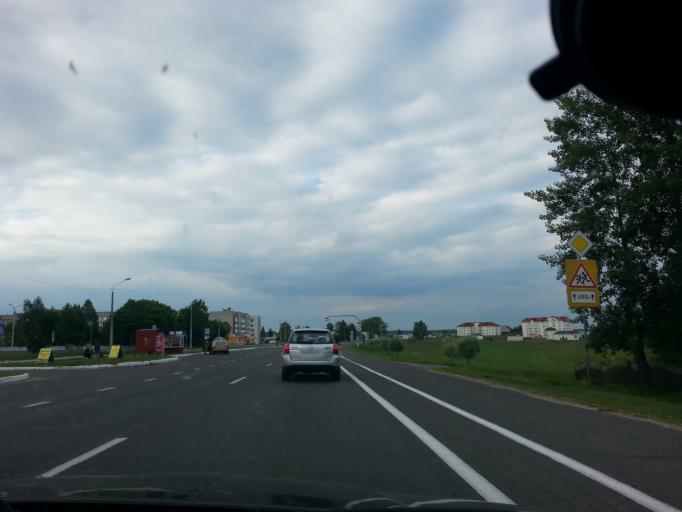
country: BY
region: Minsk
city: Myadzyel
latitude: 54.8708
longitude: 26.9367
